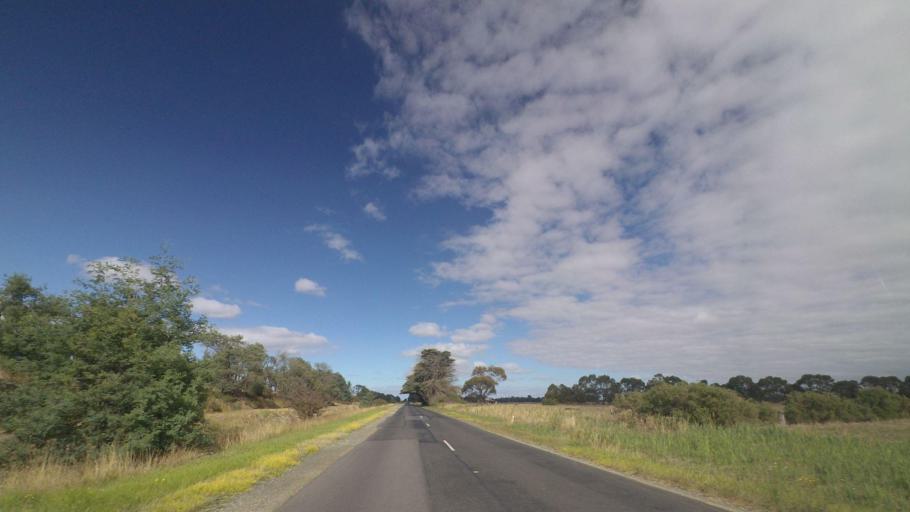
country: AU
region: Victoria
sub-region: Cardinia
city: Pakenham South
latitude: -38.1575
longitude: 145.5500
